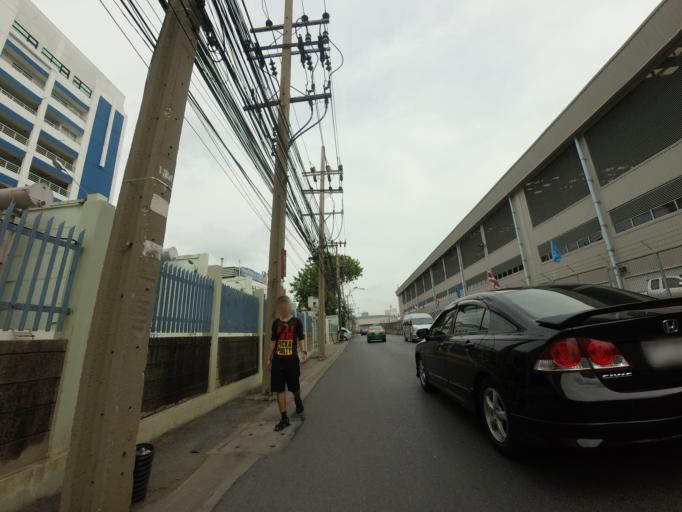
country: TH
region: Bangkok
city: Watthana
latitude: 13.7462
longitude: 100.5856
